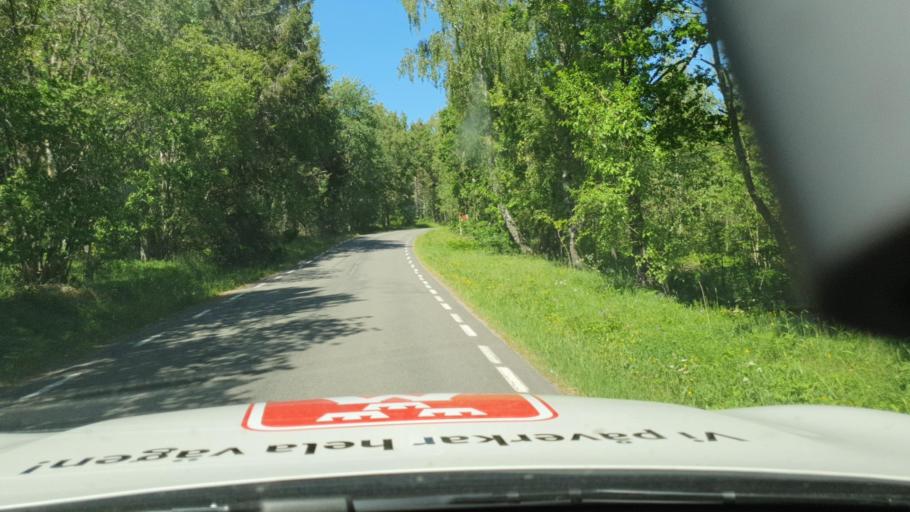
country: SE
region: Vaestra Goetaland
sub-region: Tidaholms Kommun
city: Tidaholm
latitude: 58.0991
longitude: 14.0753
